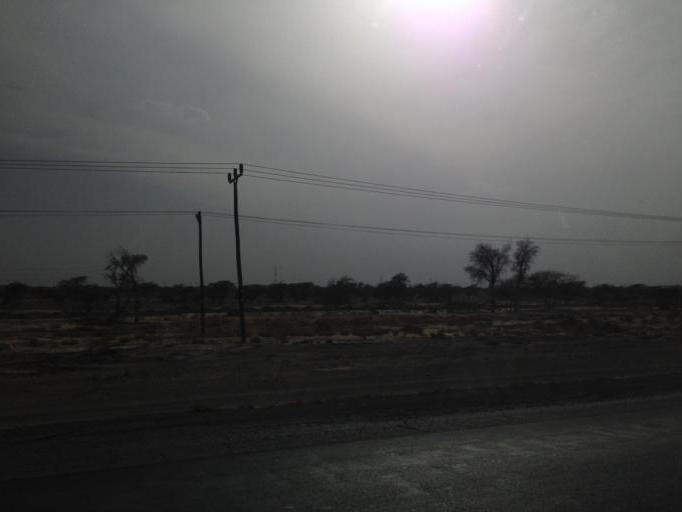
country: OM
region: Ash Sharqiyah
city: Al Qabil
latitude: 22.6008
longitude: 58.6703
